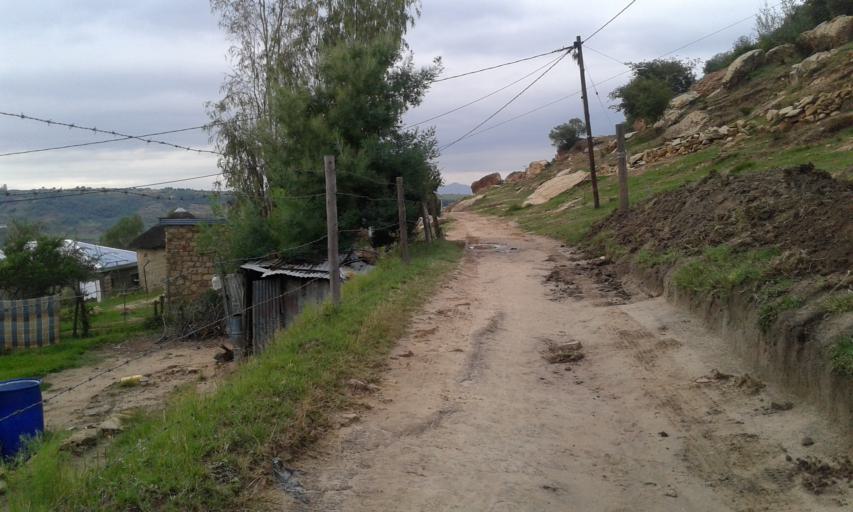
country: LS
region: Maseru
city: Maseru
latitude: -29.4210
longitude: 27.5727
